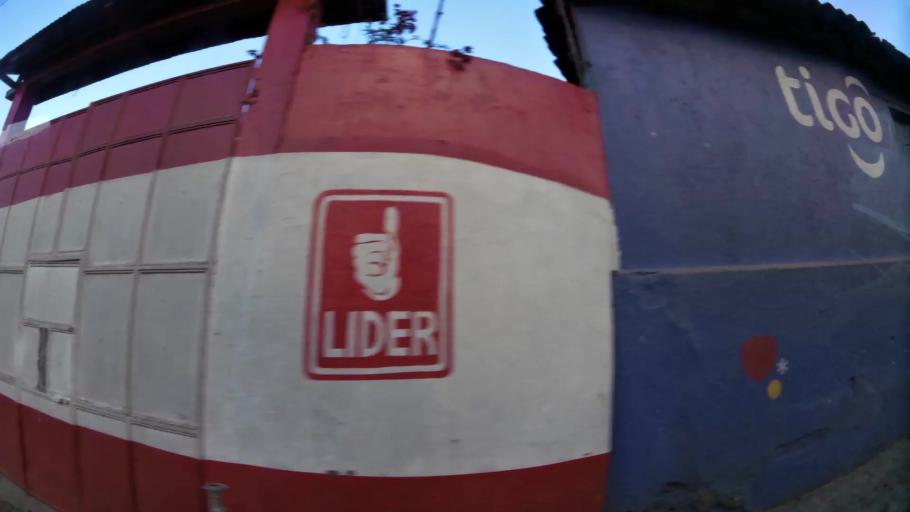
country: GT
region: Quiche
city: Chichicastenango
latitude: 14.9385
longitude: -91.1111
